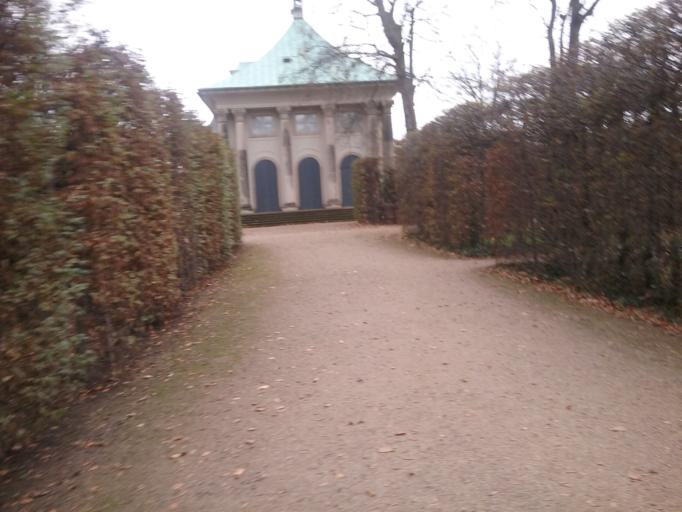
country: DE
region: Saxony
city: Heidenau
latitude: 51.0102
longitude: 13.8695
